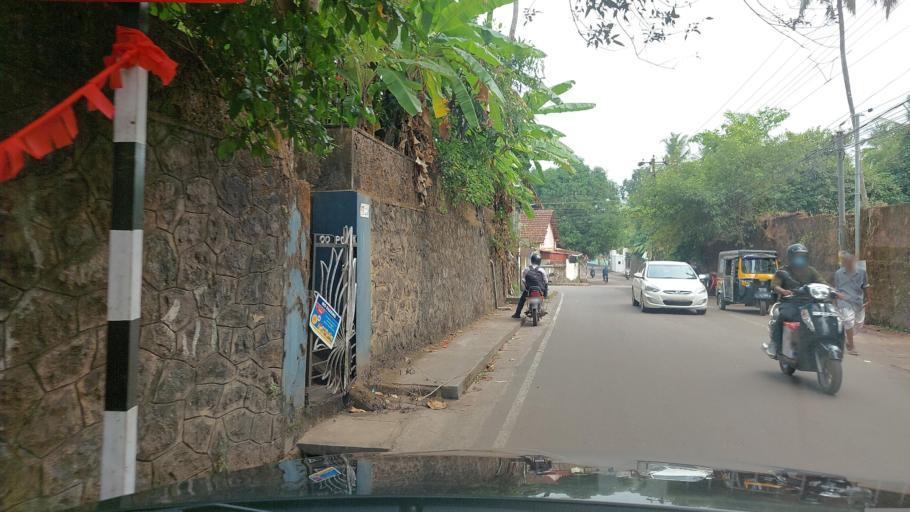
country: IN
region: Kerala
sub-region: Kozhikode
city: Kozhikode
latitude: 11.2455
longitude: 75.7880
